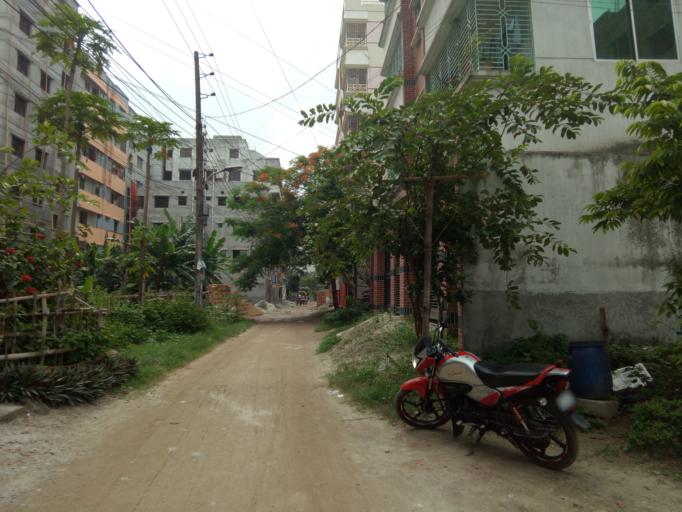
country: BD
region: Dhaka
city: Paltan
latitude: 23.7578
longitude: 90.4434
